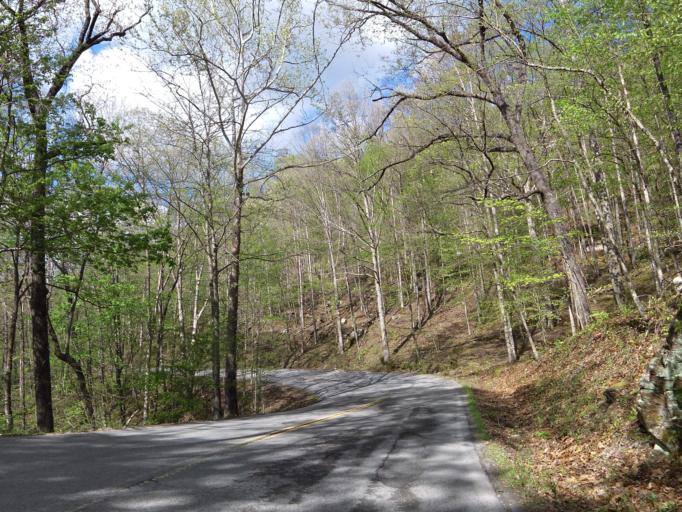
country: US
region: Kentucky
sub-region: Bell County
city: Middlesboro
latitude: 36.6181
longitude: -83.6792
